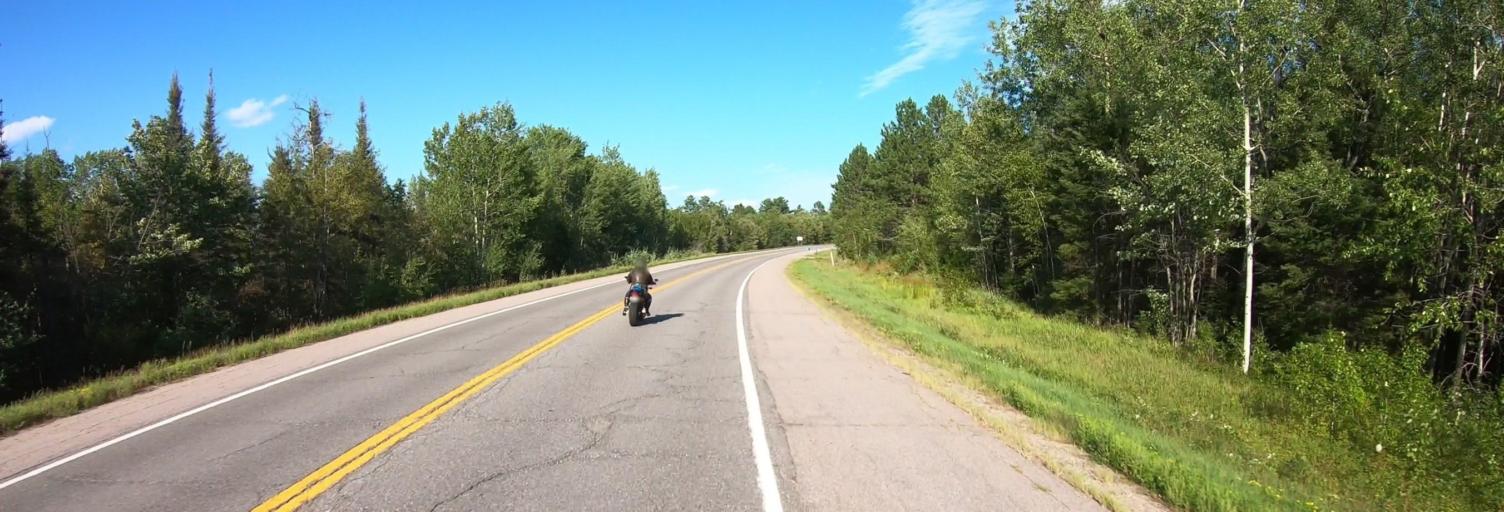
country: US
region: Minnesota
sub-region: Saint Louis County
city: Ely
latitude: 47.9277
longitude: -91.7725
